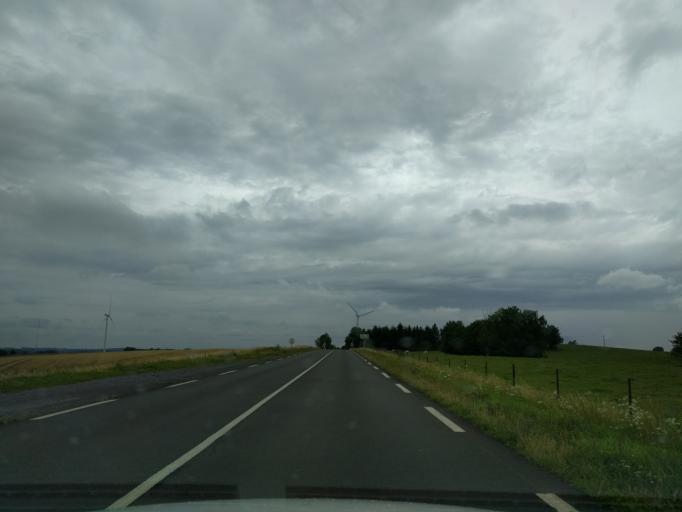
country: FR
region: Champagne-Ardenne
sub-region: Departement des Ardennes
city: Signy-le-Petit
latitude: 49.8675
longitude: 4.3030
